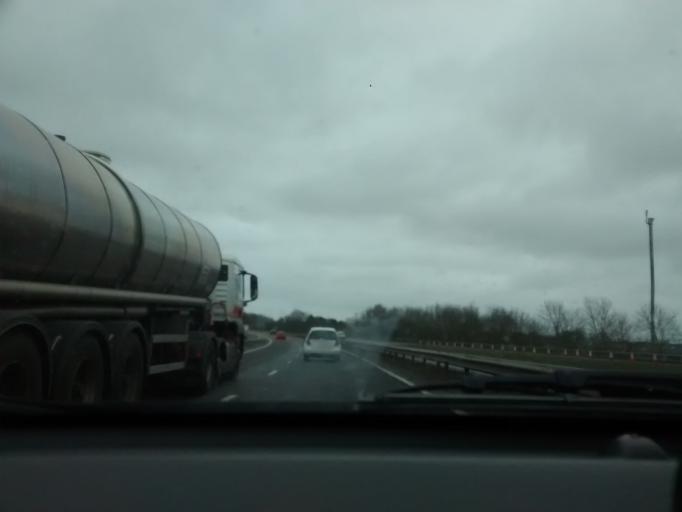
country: GB
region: England
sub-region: Suffolk
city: Bramford
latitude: 52.0340
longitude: 1.1022
